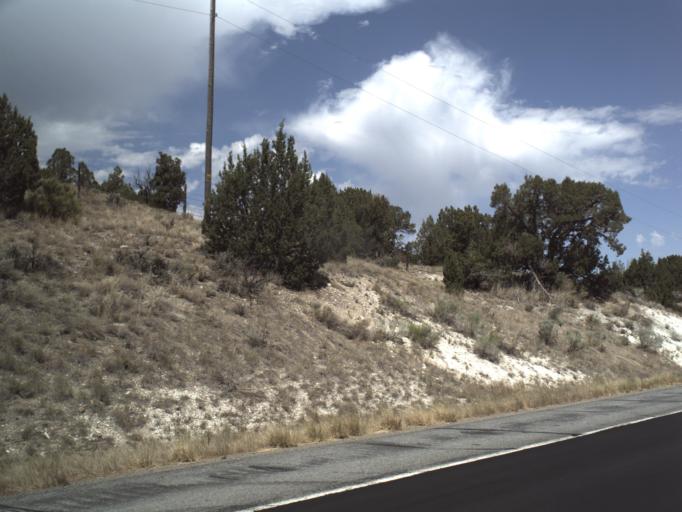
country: US
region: Utah
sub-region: Utah County
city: Eagle Mountain
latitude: 40.0160
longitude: -112.2784
